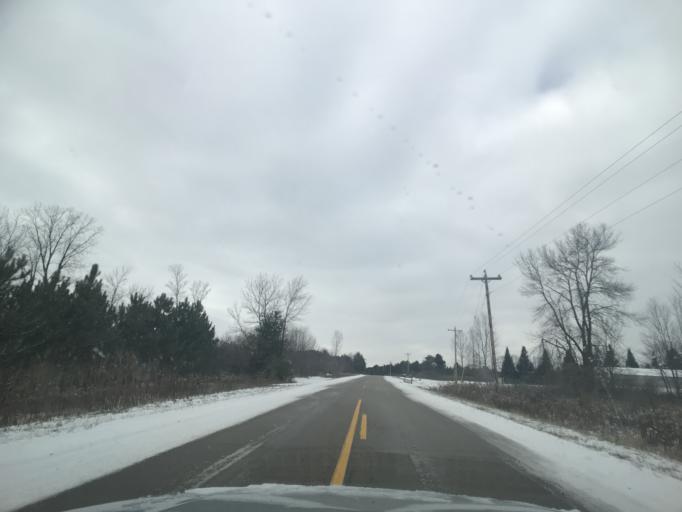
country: US
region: Wisconsin
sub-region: Brown County
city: Suamico
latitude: 44.7059
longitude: -88.0829
